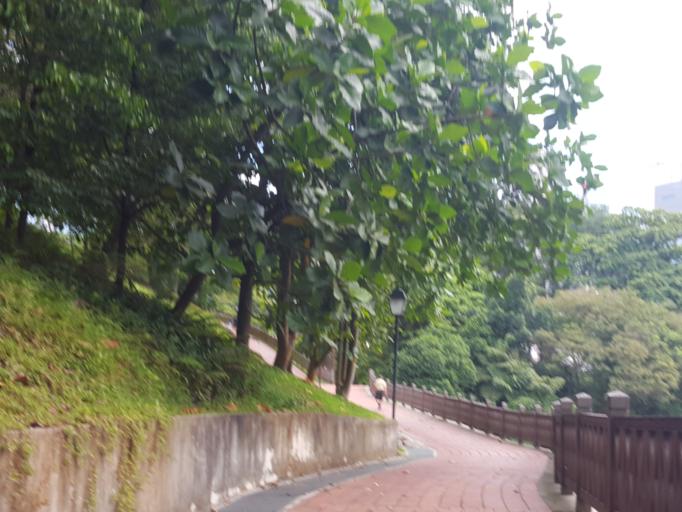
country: SG
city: Singapore
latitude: 1.2923
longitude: 103.8462
